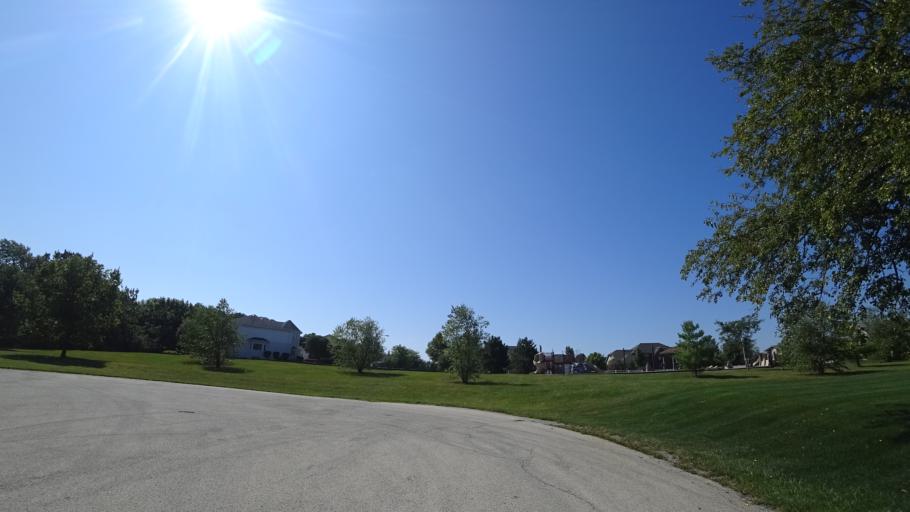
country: US
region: Illinois
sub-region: Cook County
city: Palos Heights
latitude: 41.6362
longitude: -87.8109
